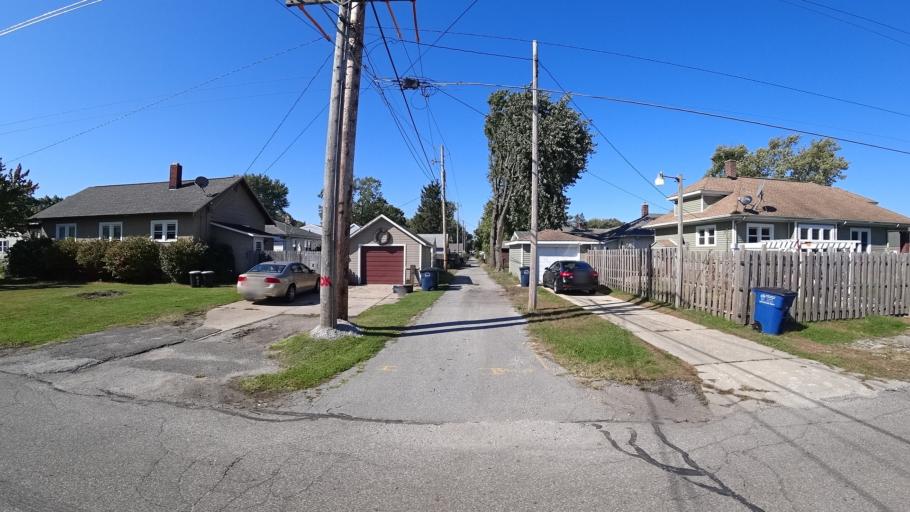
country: US
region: Indiana
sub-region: LaPorte County
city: Michigan City
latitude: 41.7034
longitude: -86.8906
